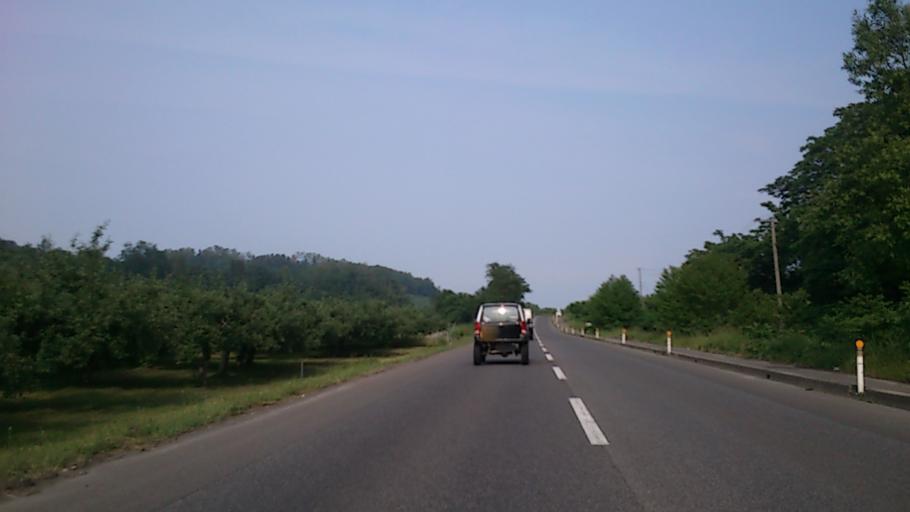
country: JP
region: Aomori
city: Hirosaki
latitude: 40.5892
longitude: 140.3769
